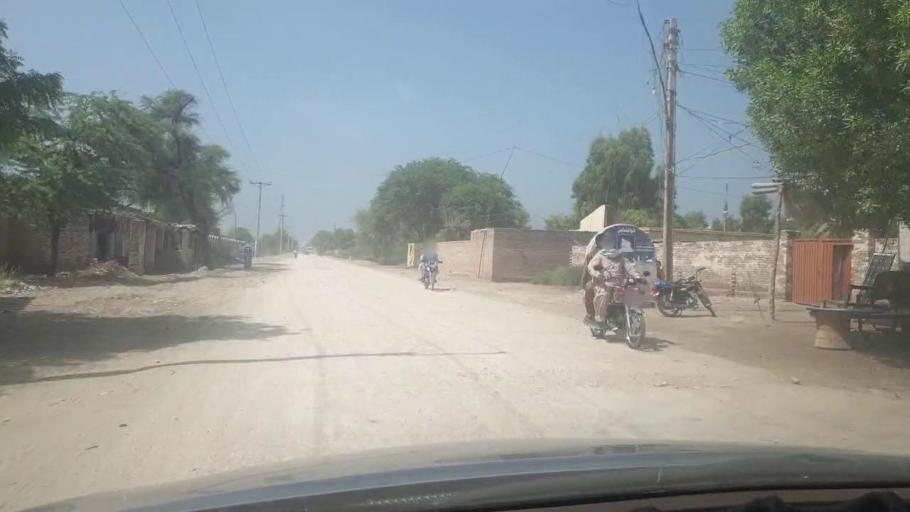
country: PK
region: Sindh
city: Ranipur
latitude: 27.2852
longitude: 68.6030
